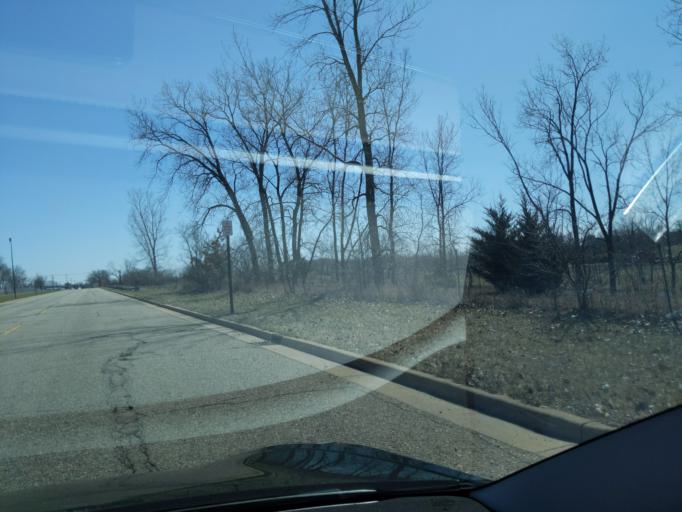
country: US
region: Michigan
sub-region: Ingham County
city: Mason
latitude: 42.5705
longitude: -84.4374
